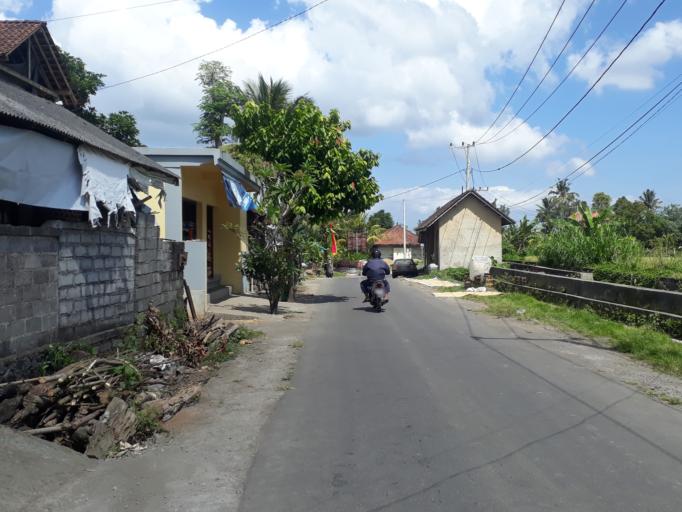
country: ID
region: Bali
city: Banjar Wangsian
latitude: -8.4725
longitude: 115.4440
